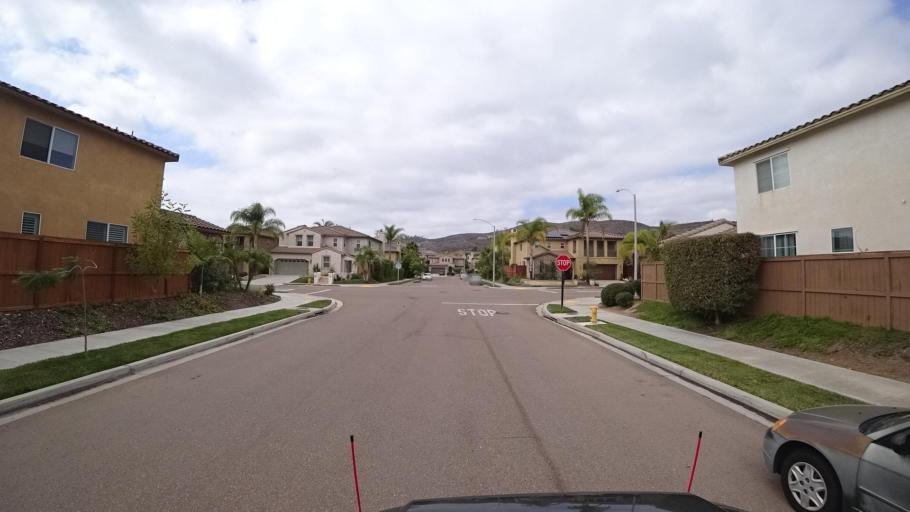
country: US
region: California
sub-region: San Diego County
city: Fairbanks Ranch
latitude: 33.0264
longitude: -117.1147
